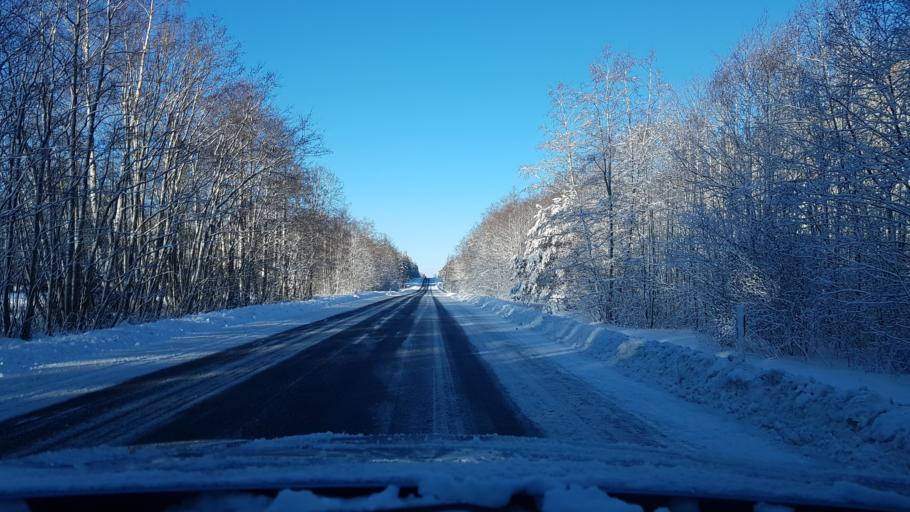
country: EE
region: Hiiumaa
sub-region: Kaerdla linn
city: Kardla
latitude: 58.9571
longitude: 22.8619
